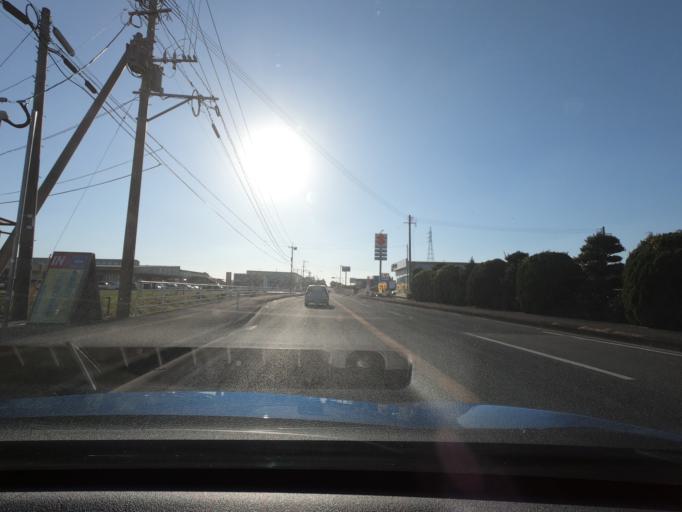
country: JP
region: Kagoshima
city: Izumi
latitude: 32.0885
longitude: 130.2860
